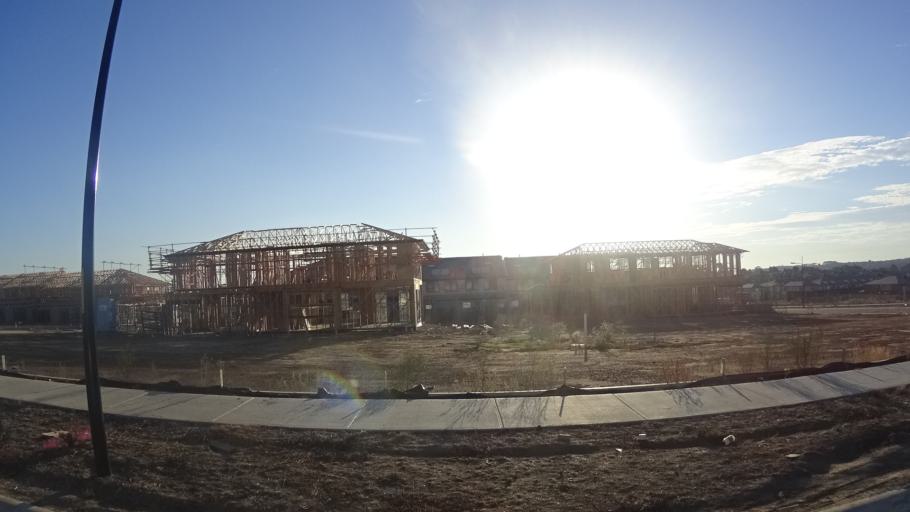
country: AU
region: Victoria
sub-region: Knox
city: Knoxfield
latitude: -37.8836
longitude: 145.2394
